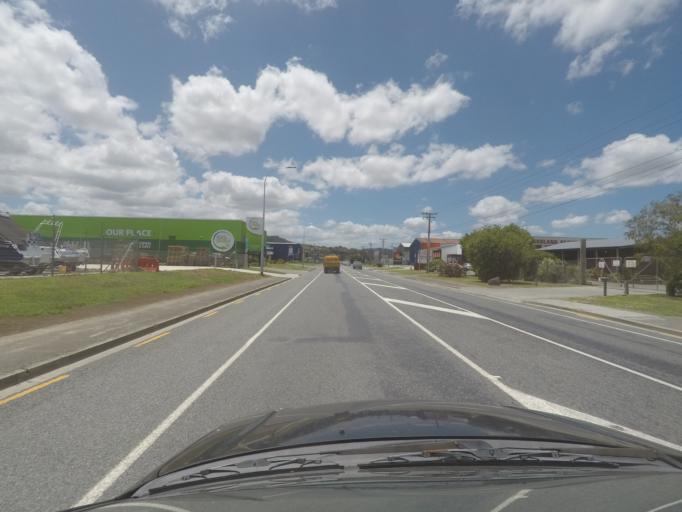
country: NZ
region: Northland
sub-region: Whangarei
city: Whangarei
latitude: -35.7414
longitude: 174.3324
